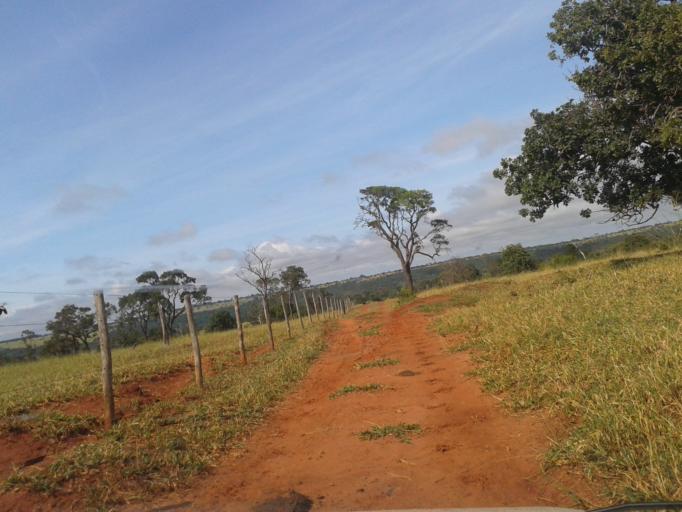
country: BR
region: Minas Gerais
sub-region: Campina Verde
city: Campina Verde
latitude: -19.4154
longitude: -49.6566
